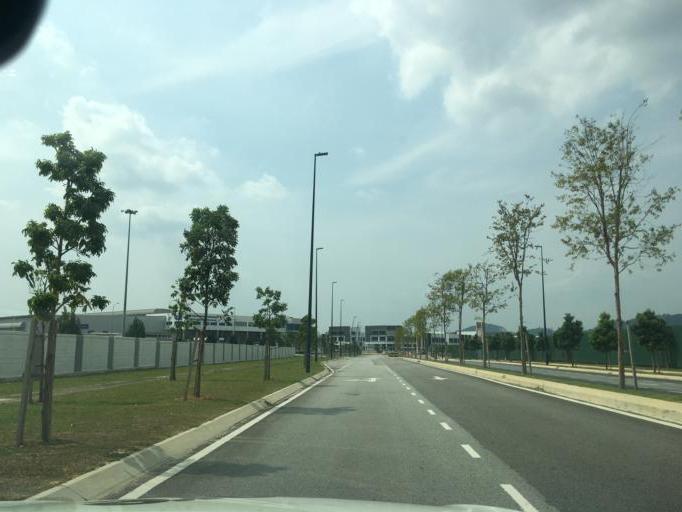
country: MY
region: Selangor
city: Klang
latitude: 3.0827
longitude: 101.4765
